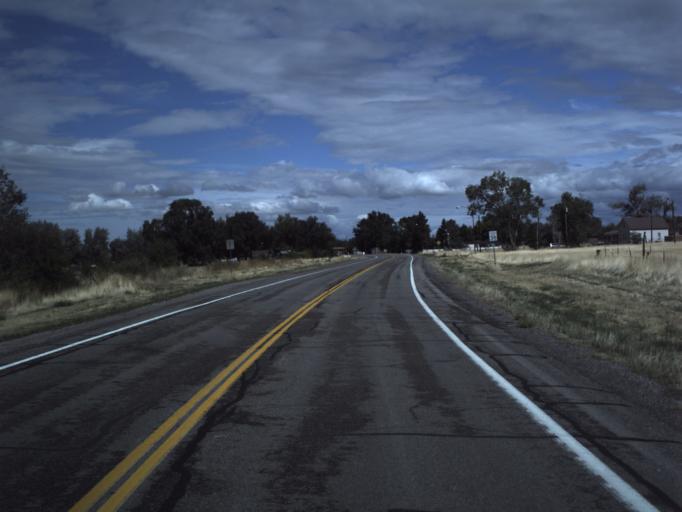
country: US
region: Utah
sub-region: Millard County
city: Fillmore
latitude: 38.8792
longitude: -112.4119
